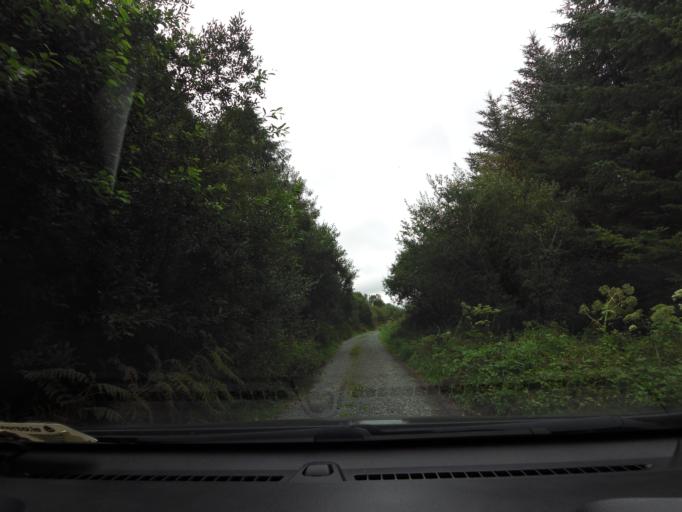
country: IE
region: Connaught
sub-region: County Galway
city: Athenry
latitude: 53.3034
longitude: -8.6658
